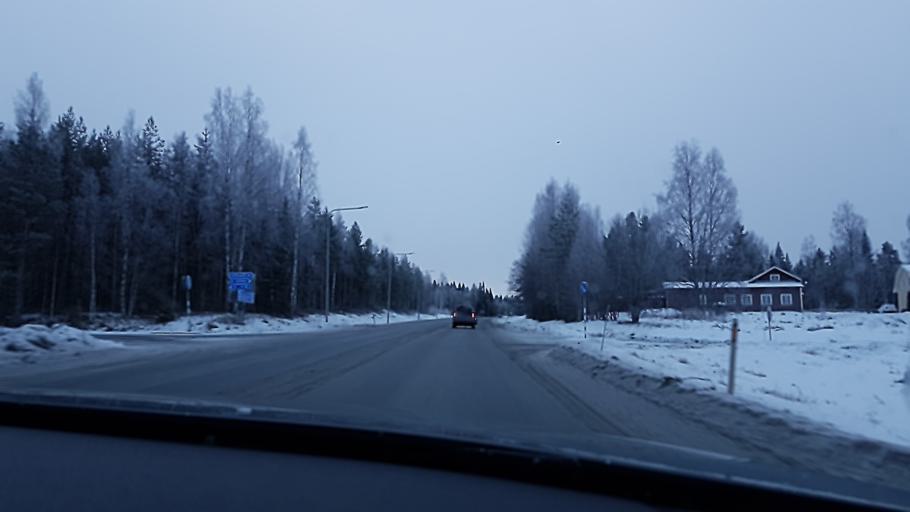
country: SE
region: Jaemtland
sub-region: OEstersunds Kommun
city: Lit
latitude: 63.3083
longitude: 14.8706
